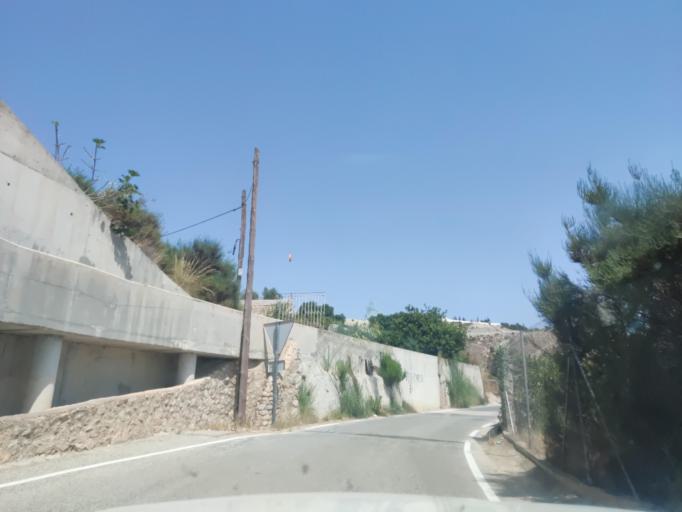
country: ES
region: Murcia
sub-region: Murcia
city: Ulea
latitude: 38.1430
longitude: -1.3225
